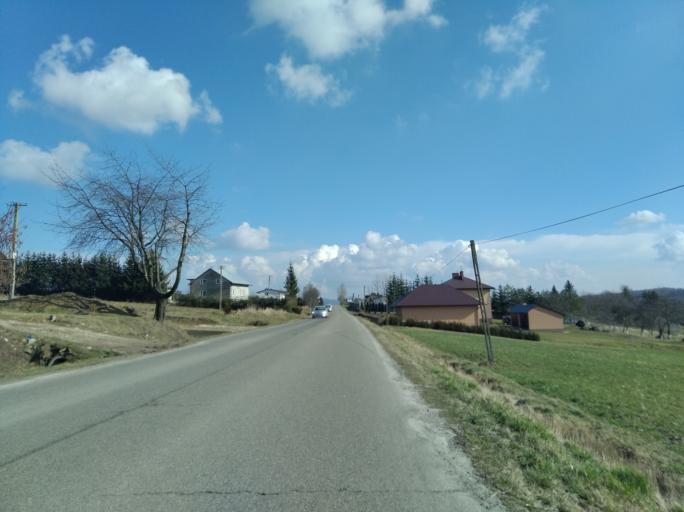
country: PL
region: Subcarpathian Voivodeship
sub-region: Powiat strzyzowski
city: Frysztak
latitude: 49.8495
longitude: 21.5348
